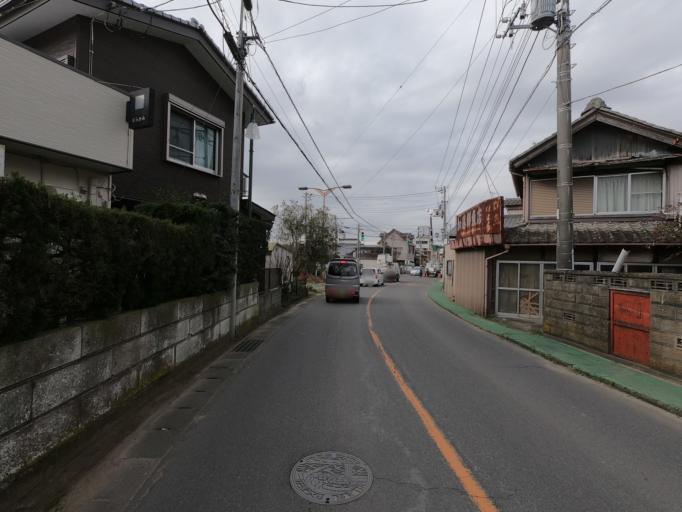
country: JP
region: Ibaraki
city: Ishioka
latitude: 36.1052
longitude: 140.4159
